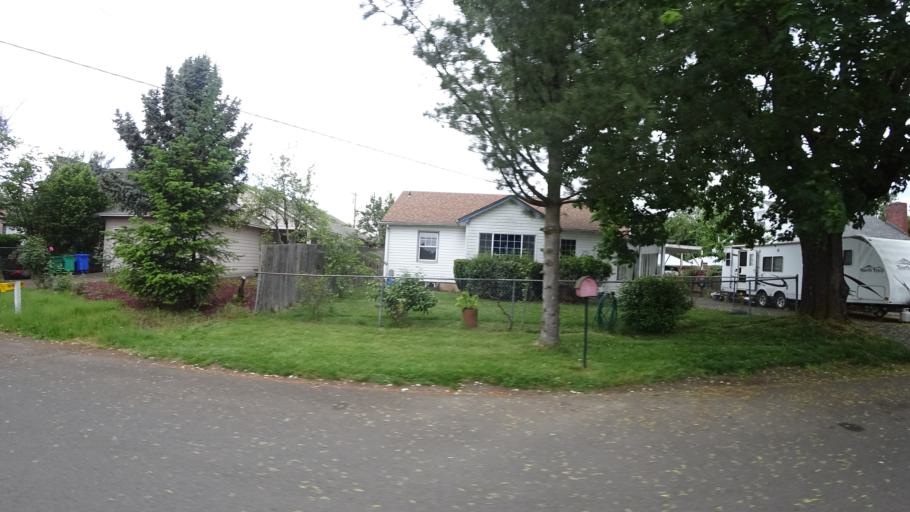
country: US
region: Oregon
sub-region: Multnomah County
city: Lents
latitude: 45.5062
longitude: -122.5547
